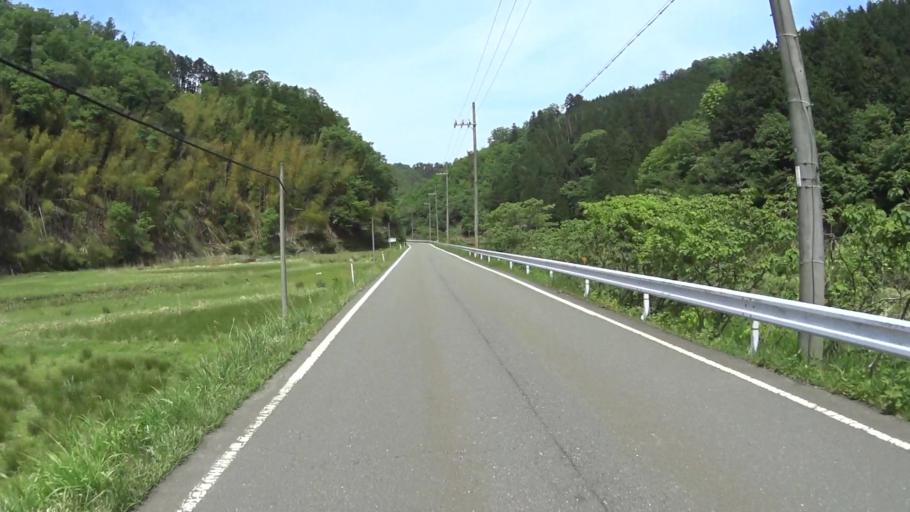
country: JP
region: Kyoto
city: Maizuru
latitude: 35.4257
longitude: 135.4769
